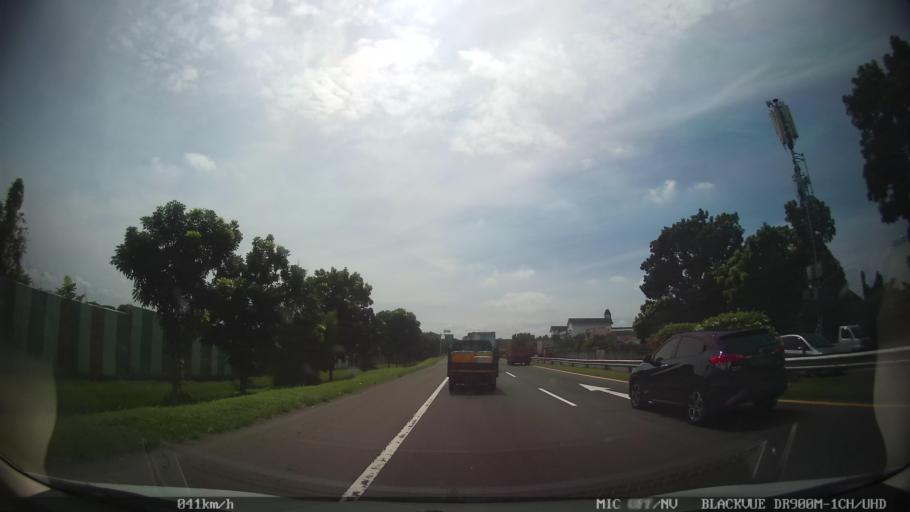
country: ID
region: North Sumatra
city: Medan
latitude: 3.6380
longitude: 98.7041
